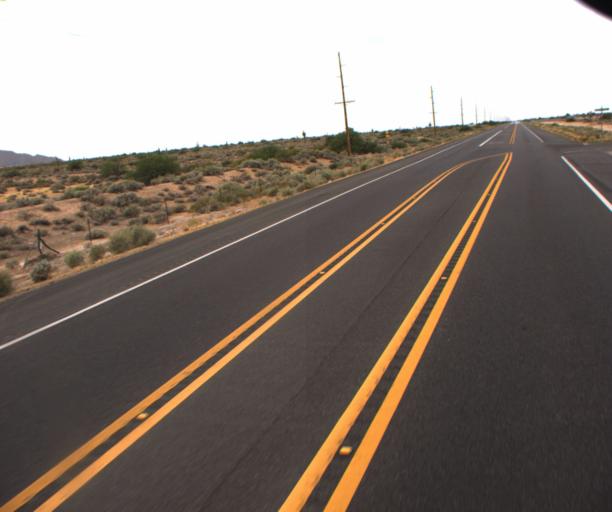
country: US
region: Arizona
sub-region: Pinal County
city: Sacaton
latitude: 33.0488
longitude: -111.6722
